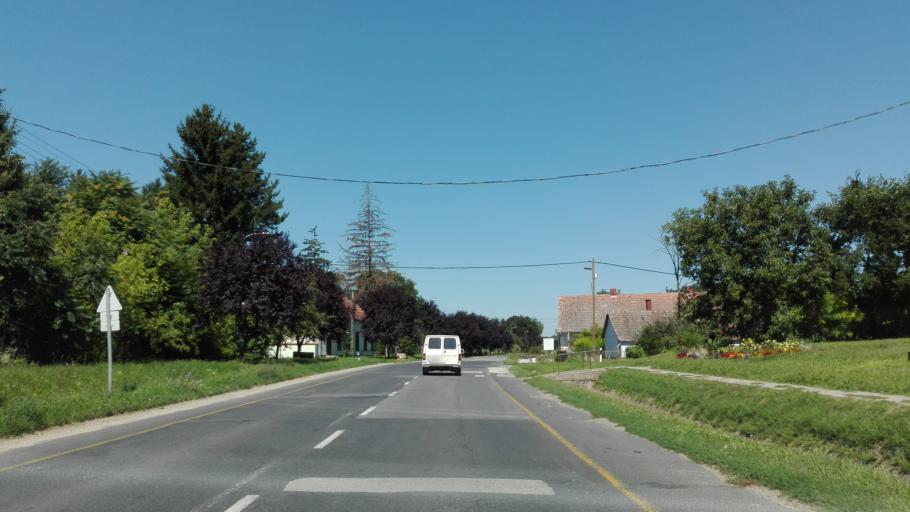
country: HU
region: Fejer
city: Mezoszilas
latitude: 46.8197
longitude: 18.4776
